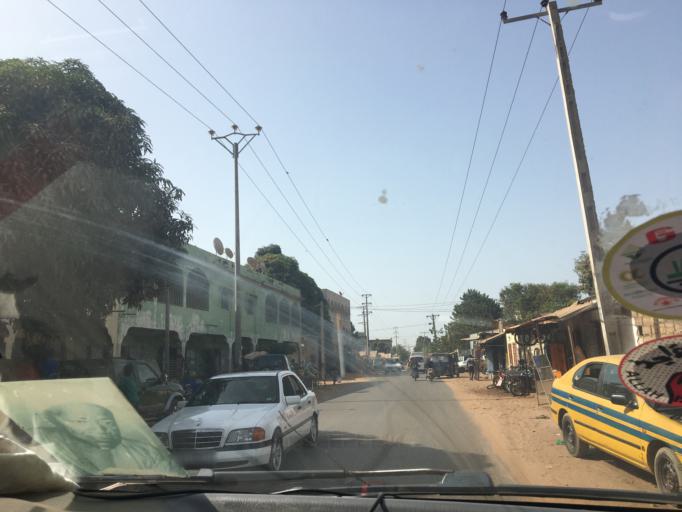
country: GM
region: Western
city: Abuko
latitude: 13.4020
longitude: -16.6733
